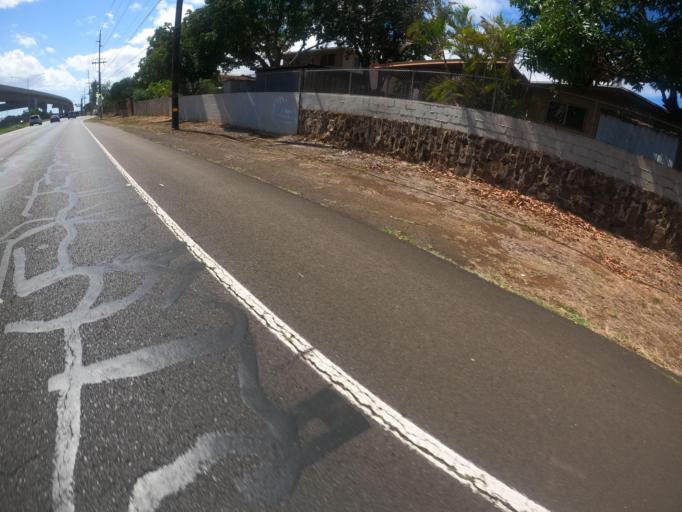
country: US
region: Hawaii
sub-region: Honolulu County
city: Waipahu
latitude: 21.3903
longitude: -157.9938
